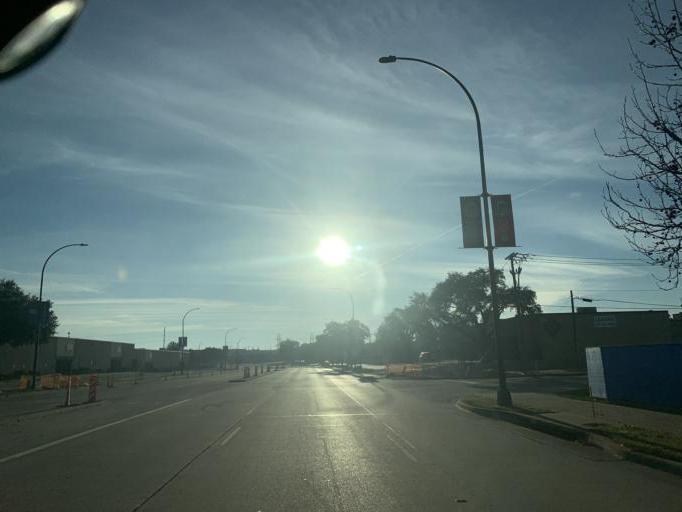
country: US
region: Texas
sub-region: Tarrant County
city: Arlington
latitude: 32.7493
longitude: -97.0790
